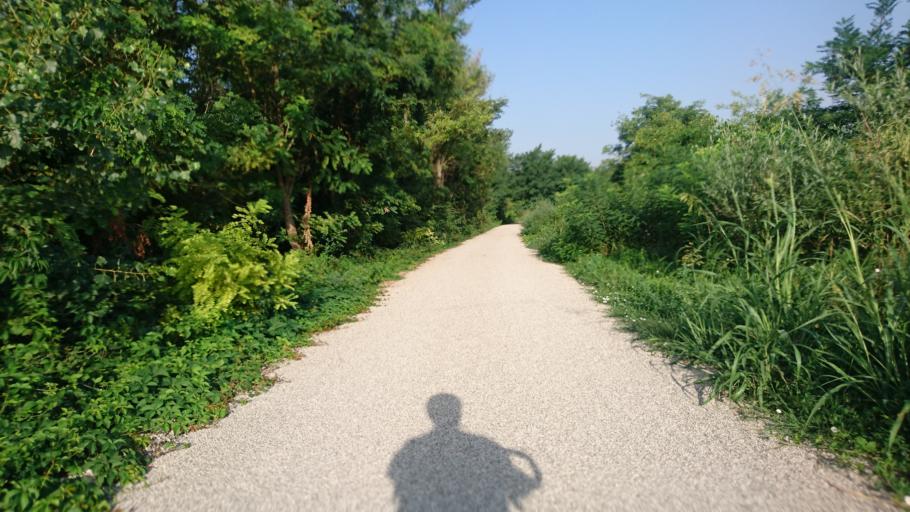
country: IT
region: Veneto
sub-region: Provincia di Padova
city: Cadoneghe
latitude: 45.4407
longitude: 11.9108
